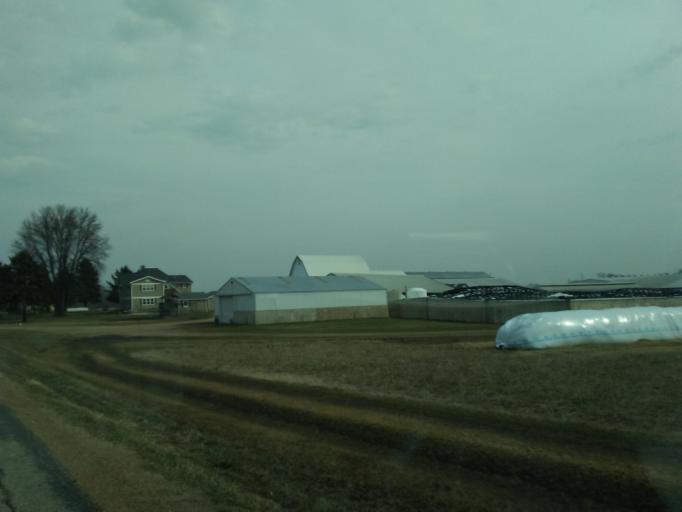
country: US
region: Wisconsin
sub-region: Dane County
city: Middleton
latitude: 43.1349
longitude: -89.4916
